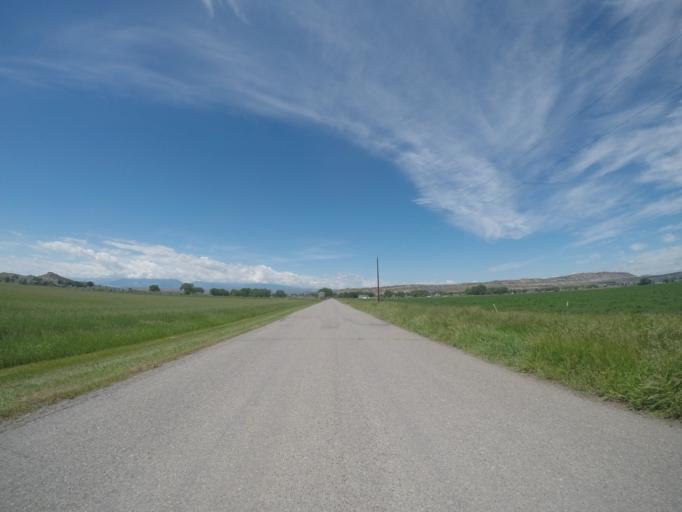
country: US
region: Montana
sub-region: Carbon County
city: Red Lodge
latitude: 45.2577
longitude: -108.8965
